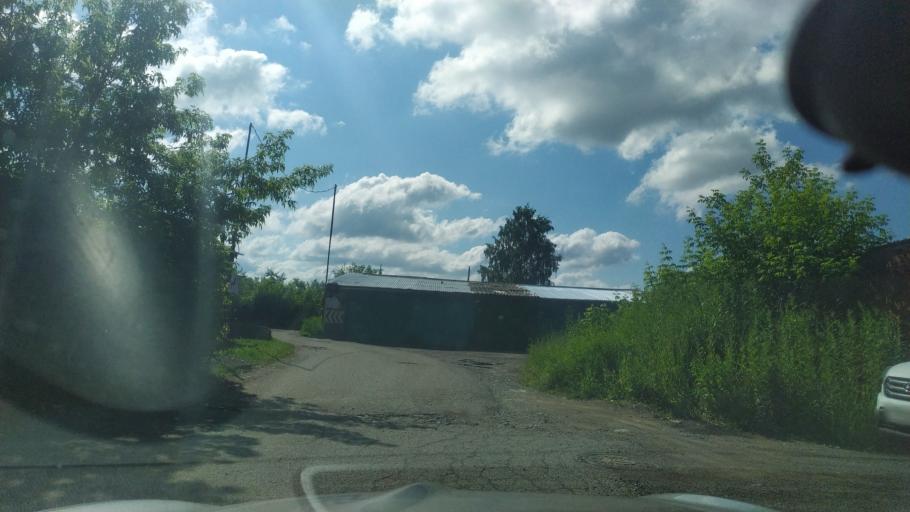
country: RU
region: Moscow
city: Vostochnyy
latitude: 55.8139
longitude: 37.8654
